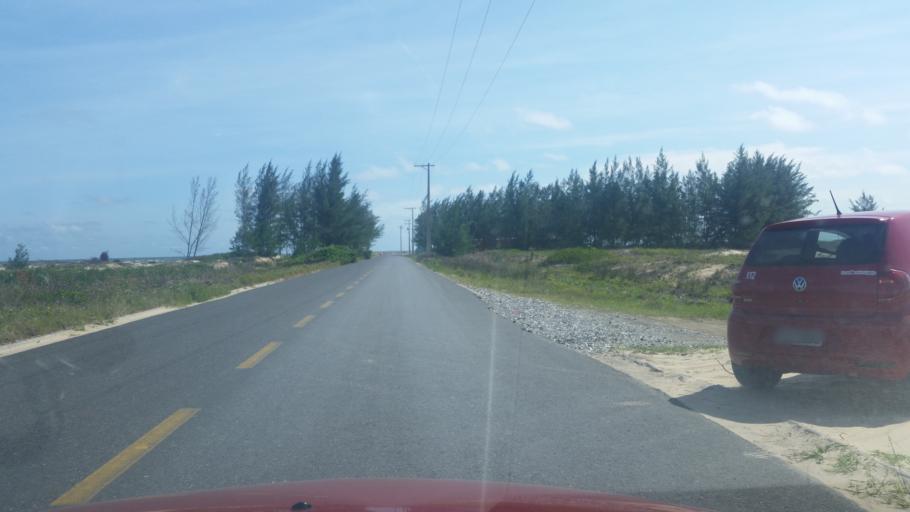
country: BR
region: Sao Paulo
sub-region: Iguape
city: Iguape
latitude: -24.7056
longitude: -47.4709
